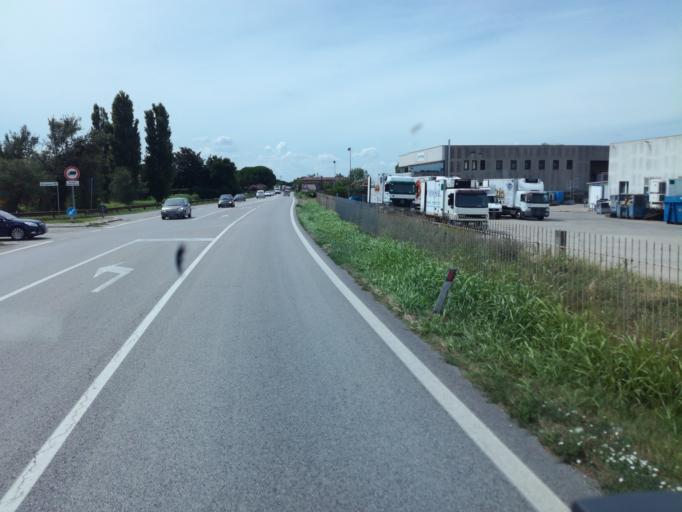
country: IT
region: Veneto
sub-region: Provincia di Rovigo
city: Rosolina
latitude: 45.0830
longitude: 12.2495
